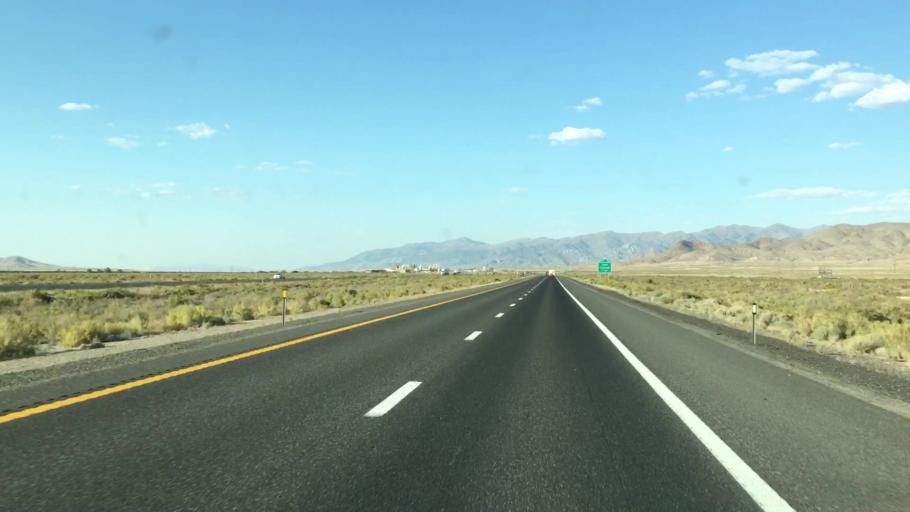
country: US
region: Nevada
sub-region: Pershing County
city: Lovelock
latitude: 40.2255
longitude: -118.4059
